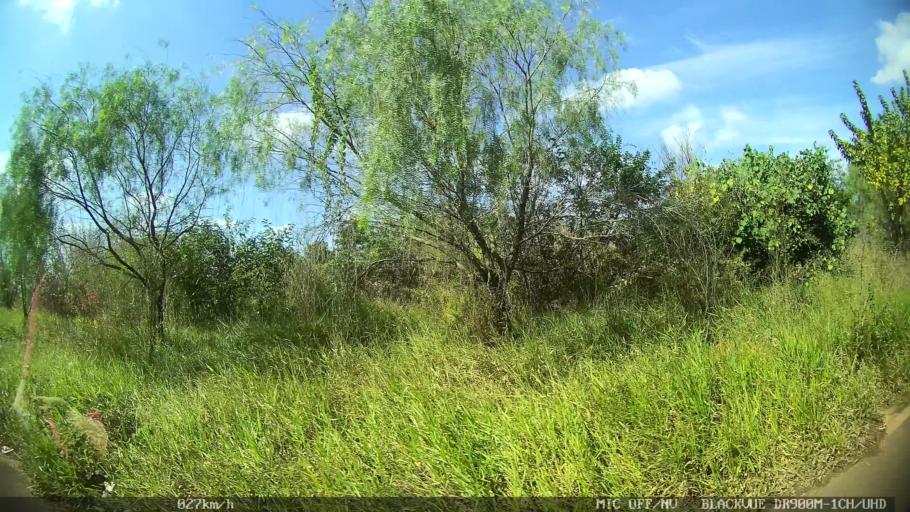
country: BR
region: Sao Paulo
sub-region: Hortolandia
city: Hortolandia
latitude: -22.8679
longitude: -47.2384
